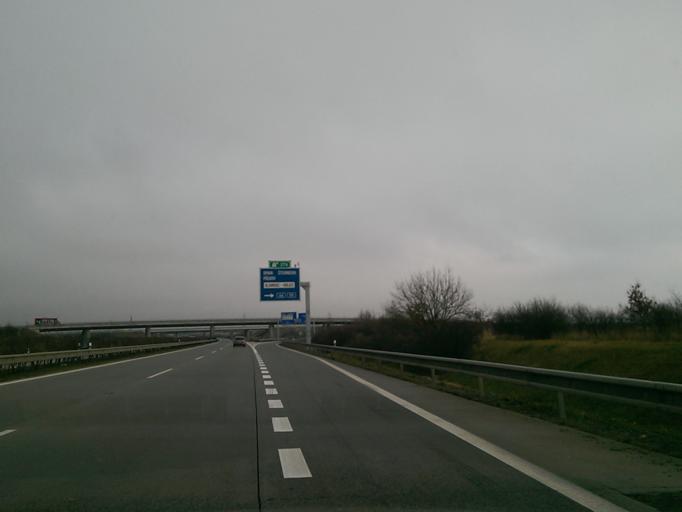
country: CZ
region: Olomoucky
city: Grygov
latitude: 49.5580
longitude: 17.3084
